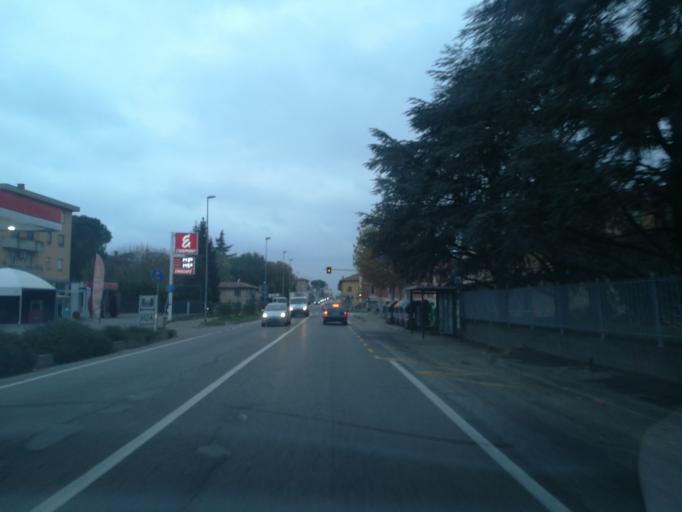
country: IT
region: Emilia-Romagna
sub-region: Provincia di Bologna
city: Toscanella
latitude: 44.3816
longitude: 11.6415
